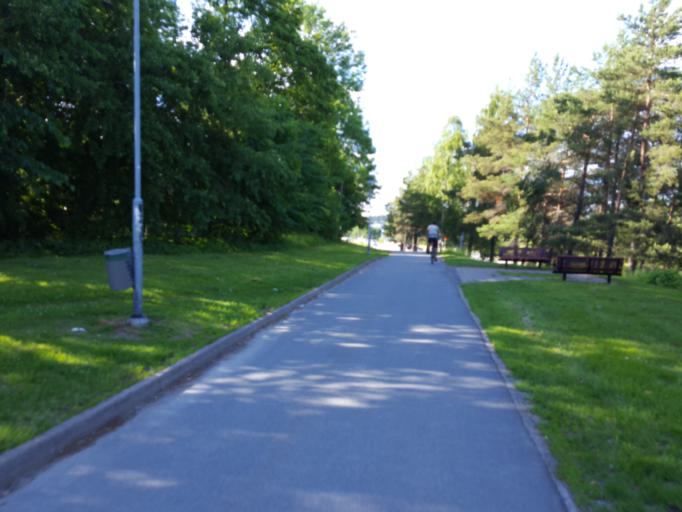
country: SE
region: Stockholm
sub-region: Upplands Vasby Kommun
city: Upplands Vaesby
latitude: 59.4682
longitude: 17.9192
